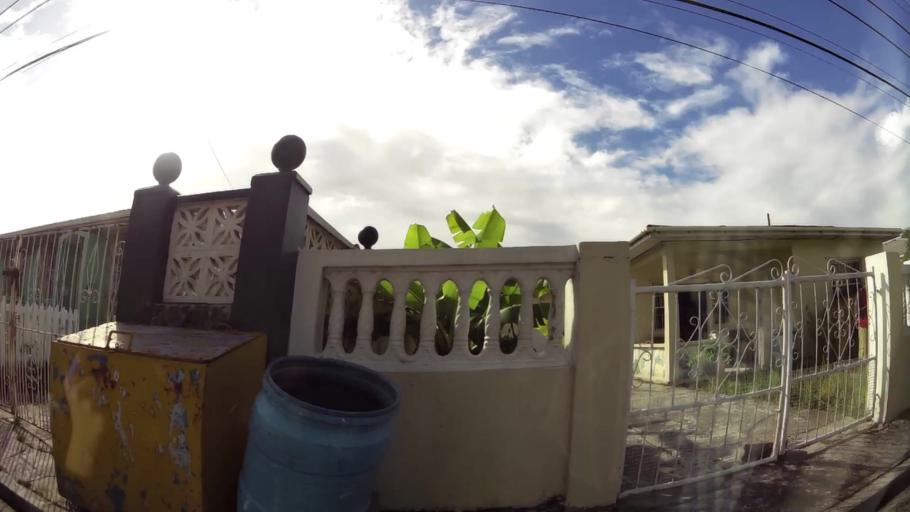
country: AG
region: Saint John
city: Saint John's
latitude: 17.1217
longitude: -61.8281
